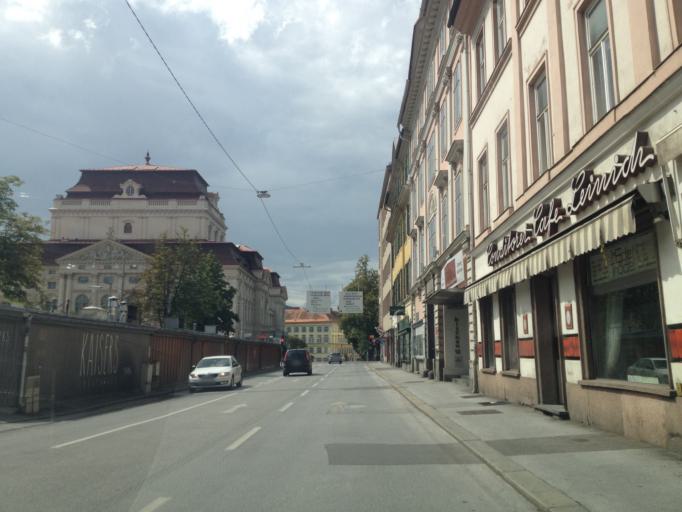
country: AT
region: Styria
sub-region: Graz Stadt
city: Graz
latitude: 47.0686
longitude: 15.4475
